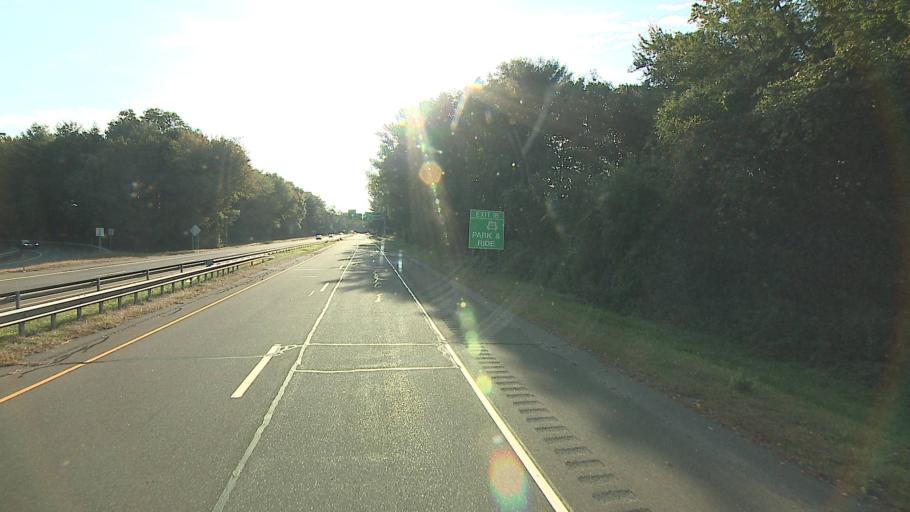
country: US
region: Connecticut
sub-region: New Haven County
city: City of Milford (balance)
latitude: 41.2329
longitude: -73.0680
